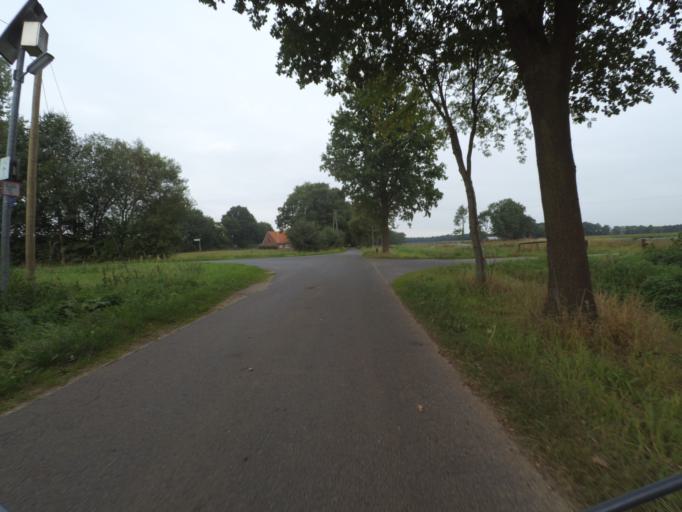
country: DE
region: Lower Saxony
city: Isterberg
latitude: 52.3318
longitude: 7.0625
